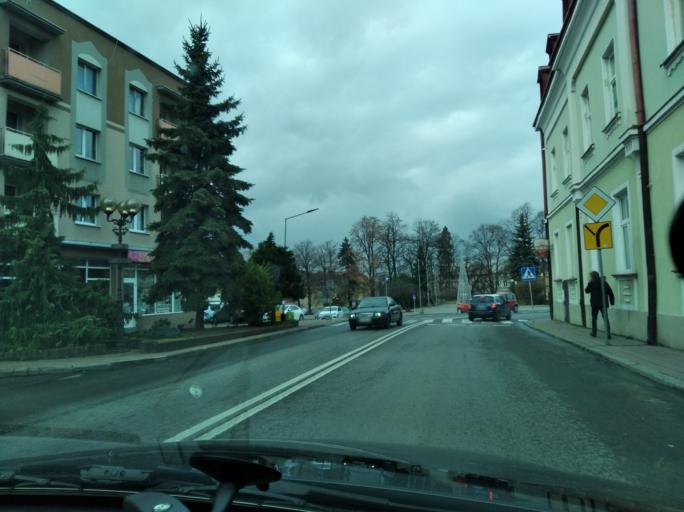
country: PL
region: Subcarpathian Voivodeship
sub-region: Powiat lancucki
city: Lancut
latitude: 50.0678
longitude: 22.2298
